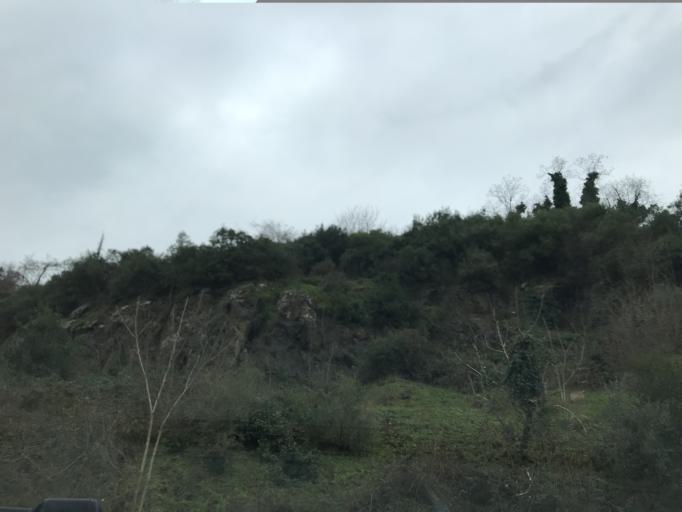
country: TR
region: Yalova
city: Termal
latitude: 40.6006
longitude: 29.1754
